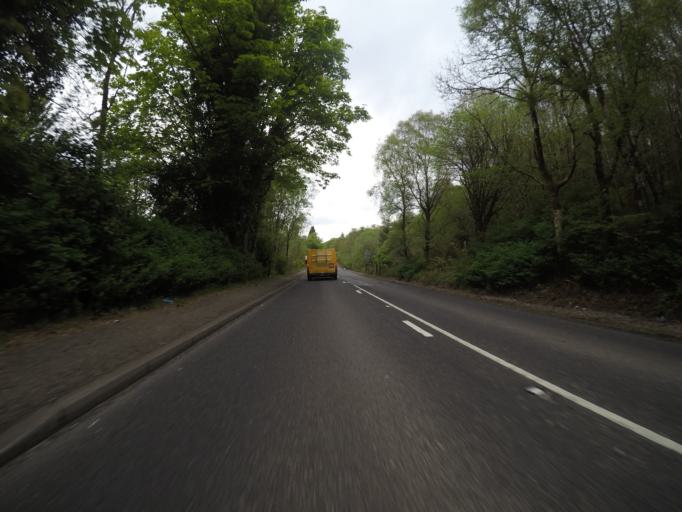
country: GB
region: Scotland
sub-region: Highland
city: Fort William
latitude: 56.7783
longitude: -5.1644
